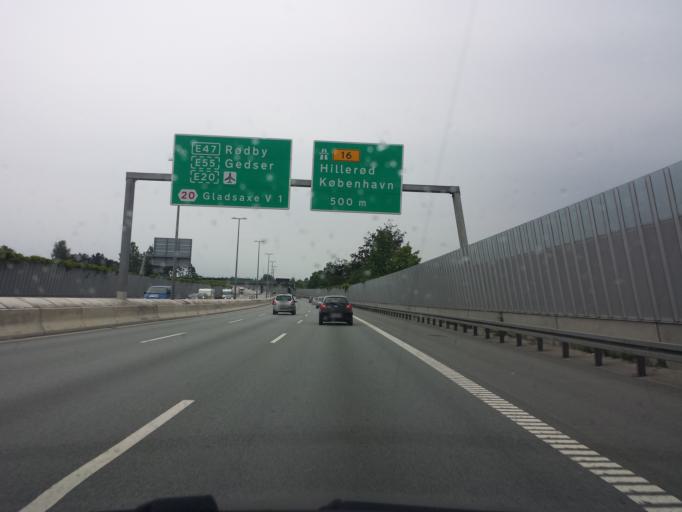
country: DK
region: Capital Region
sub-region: Gladsaxe Municipality
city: Buddinge
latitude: 55.7477
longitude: 12.4666
